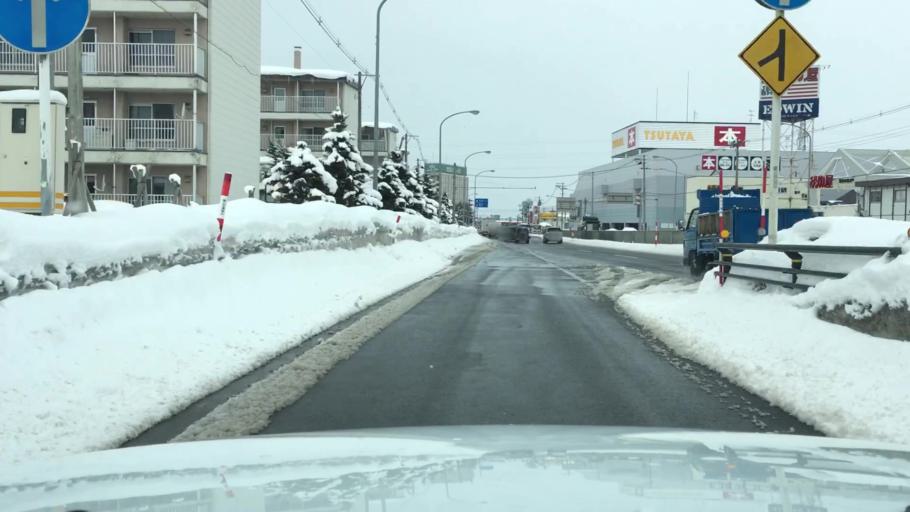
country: JP
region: Aomori
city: Hirosaki
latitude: 40.5991
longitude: 140.5016
